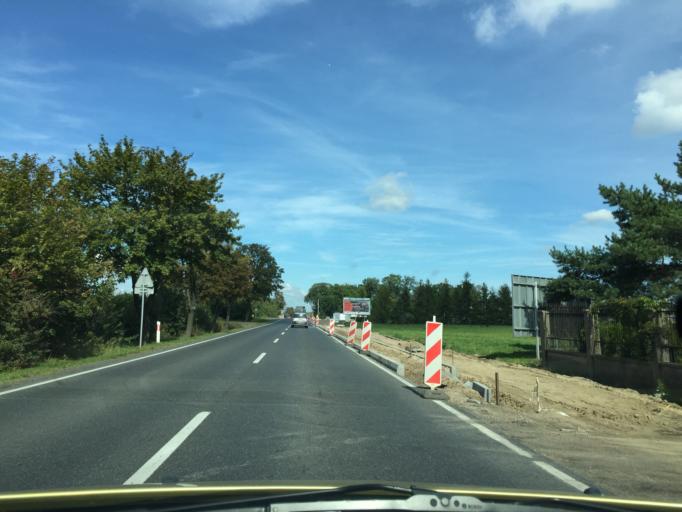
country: PL
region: Greater Poland Voivodeship
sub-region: Kalisz
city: Kalisz
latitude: 51.7931
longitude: 18.0911
